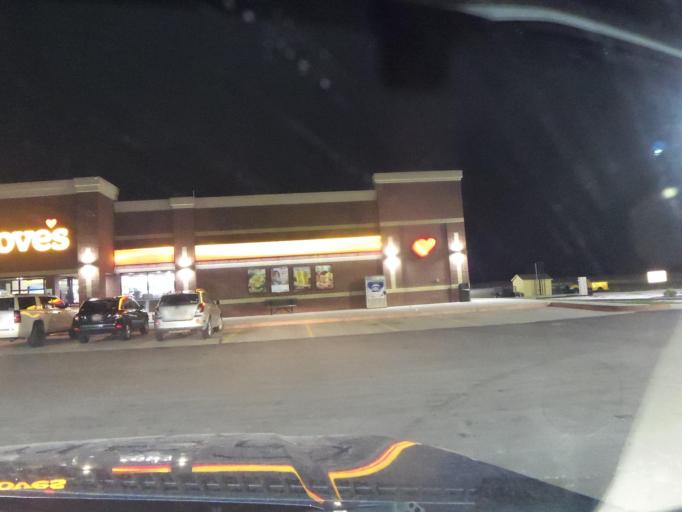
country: US
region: Missouri
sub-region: Clinton County
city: Cameron
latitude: 39.7324
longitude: -94.2184
